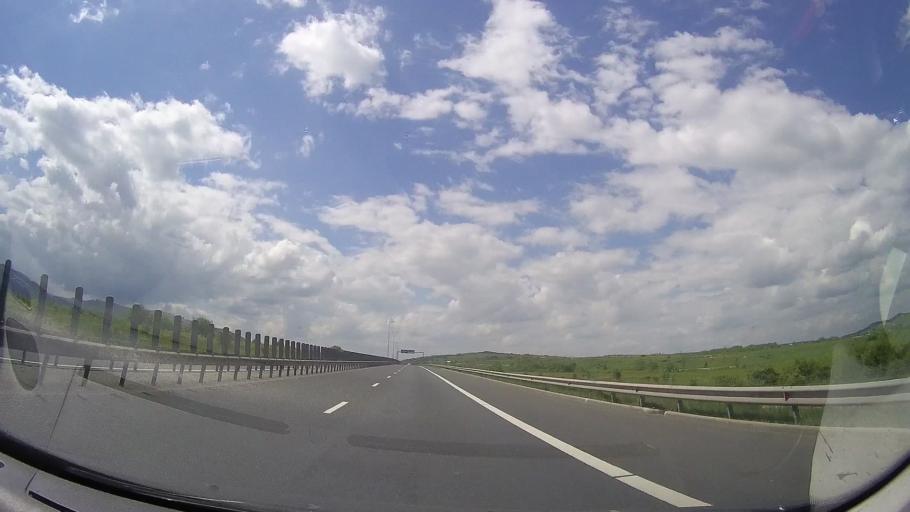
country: RO
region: Sibiu
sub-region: Oras Saliste
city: Saliste
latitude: 45.8055
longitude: 23.9130
